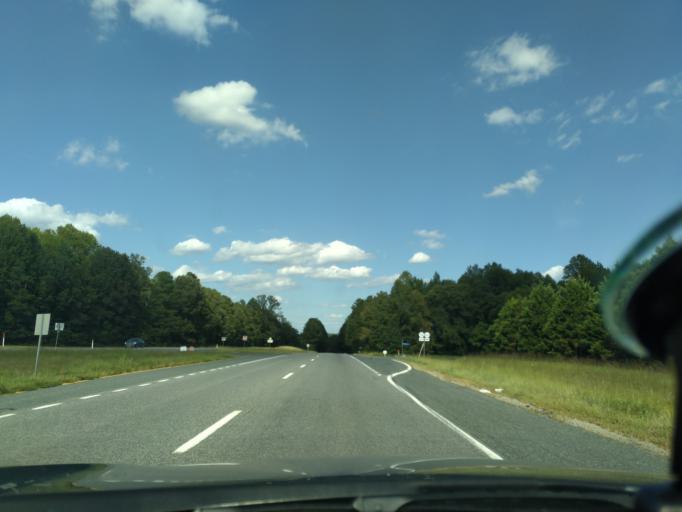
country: US
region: Virginia
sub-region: Caroline County
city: Bowling Green
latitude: 37.9622
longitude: -77.4348
